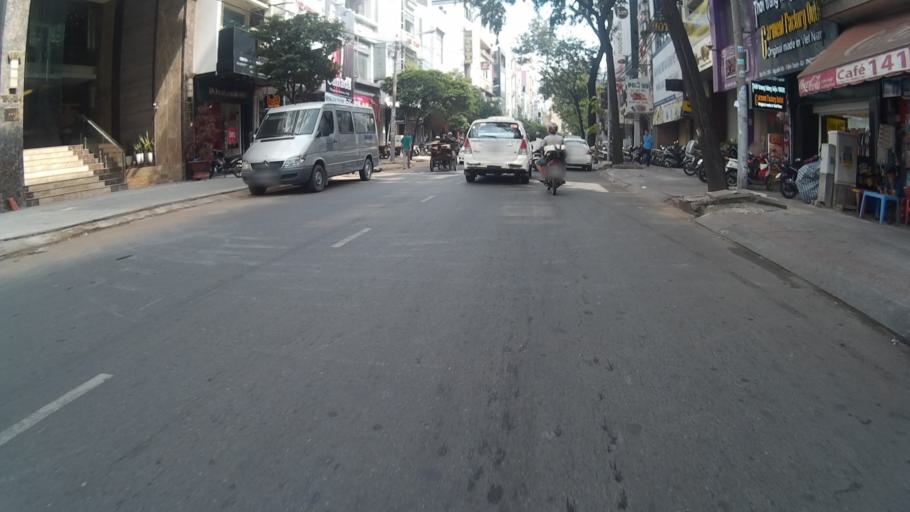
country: VN
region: Ho Chi Minh City
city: Quan Ba
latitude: 10.7686
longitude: 106.6899
